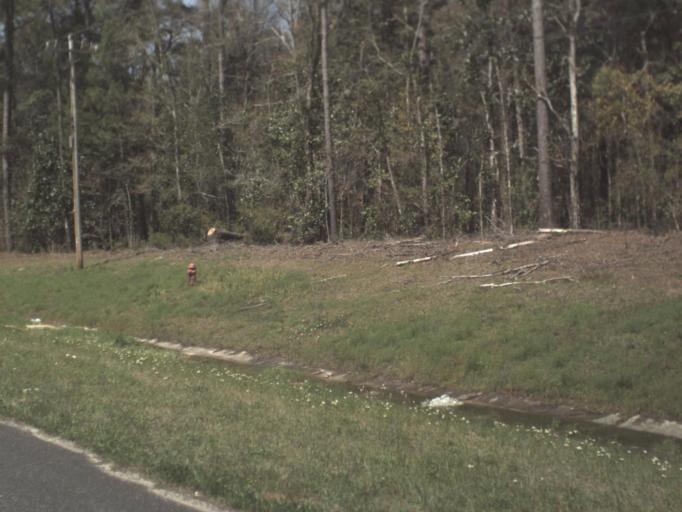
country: US
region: Florida
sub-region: Gadsden County
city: Midway
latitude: 30.5149
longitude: -84.4613
